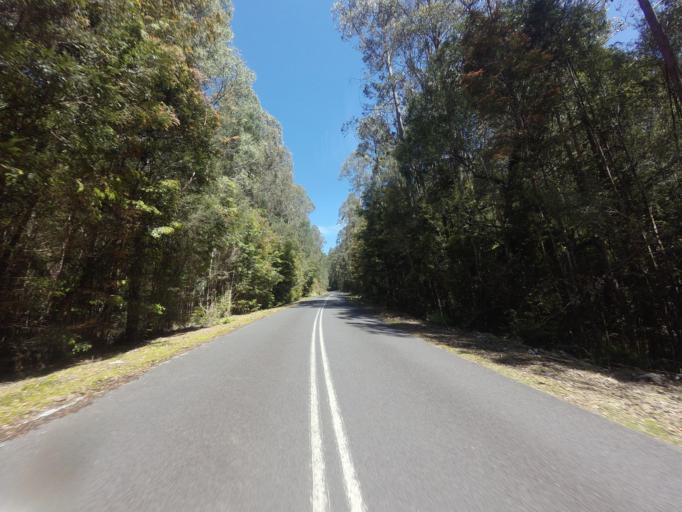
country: AU
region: Tasmania
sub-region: Huon Valley
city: Geeveston
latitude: -42.8236
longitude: 146.3323
